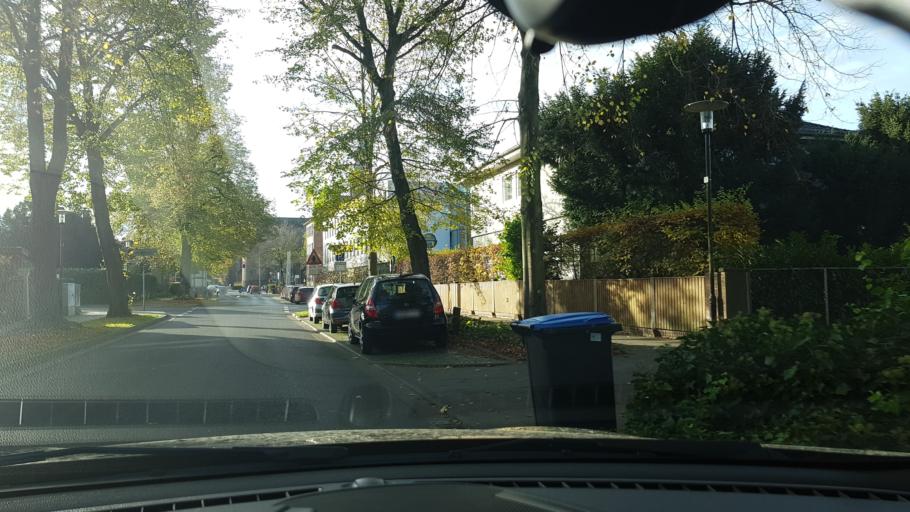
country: DE
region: North Rhine-Westphalia
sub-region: Regierungsbezirk Dusseldorf
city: Grevenbroich
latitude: 51.0910
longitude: 6.5919
